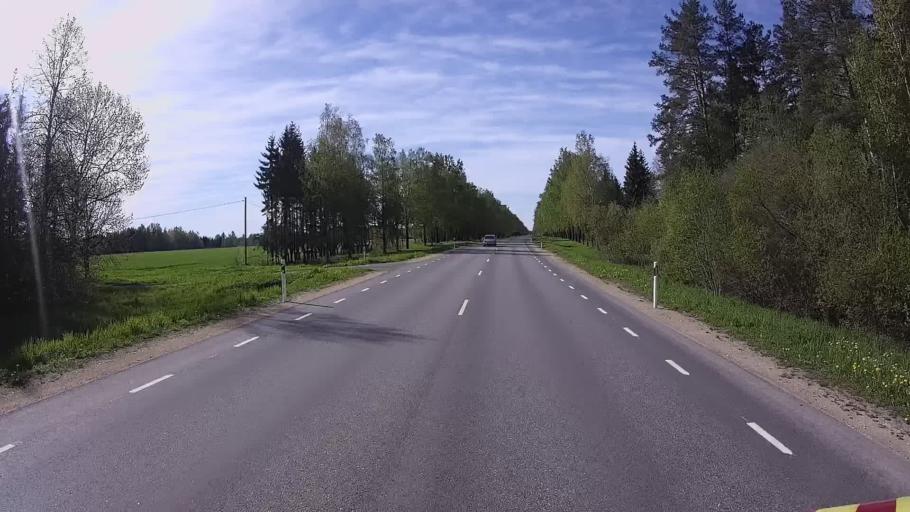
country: EE
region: Polvamaa
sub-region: Polva linn
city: Polva
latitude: 58.3043
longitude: 27.0009
